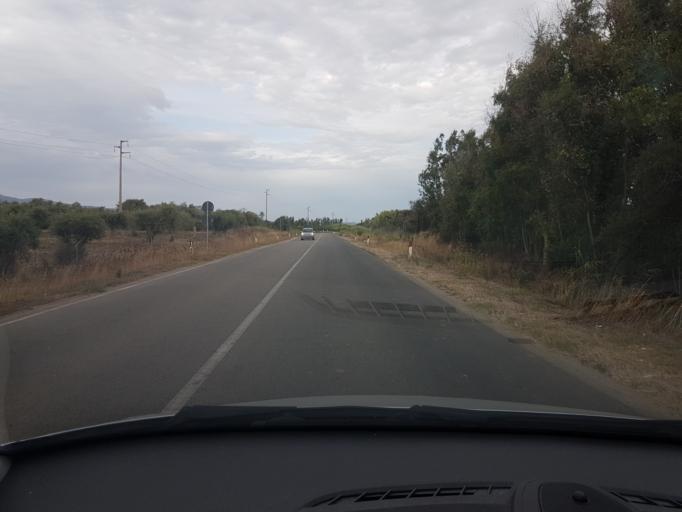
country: IT
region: Sardinia
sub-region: Provincia di Oristano
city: Riola Sardo
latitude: 40.0033
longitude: 8.5348
